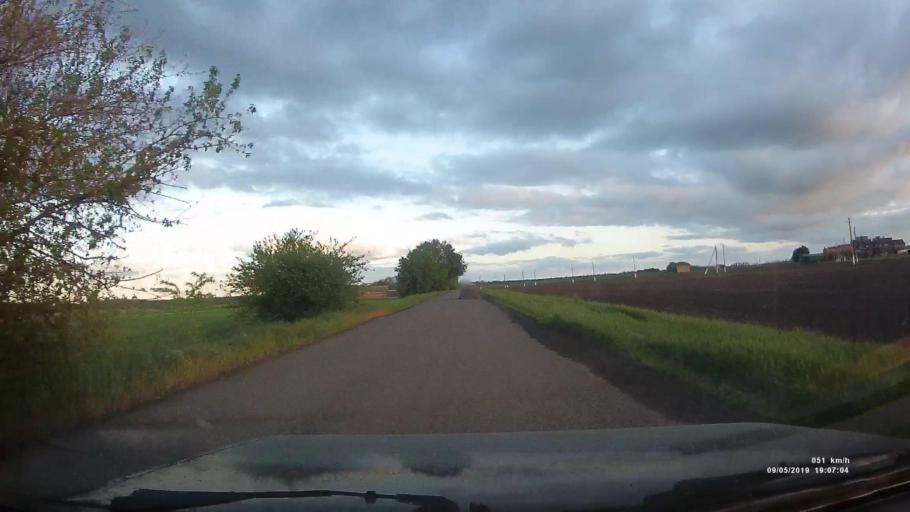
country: RU
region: Krasnodarskiy
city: Kanelovskaya
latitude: 46.7363
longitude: 39.1962
